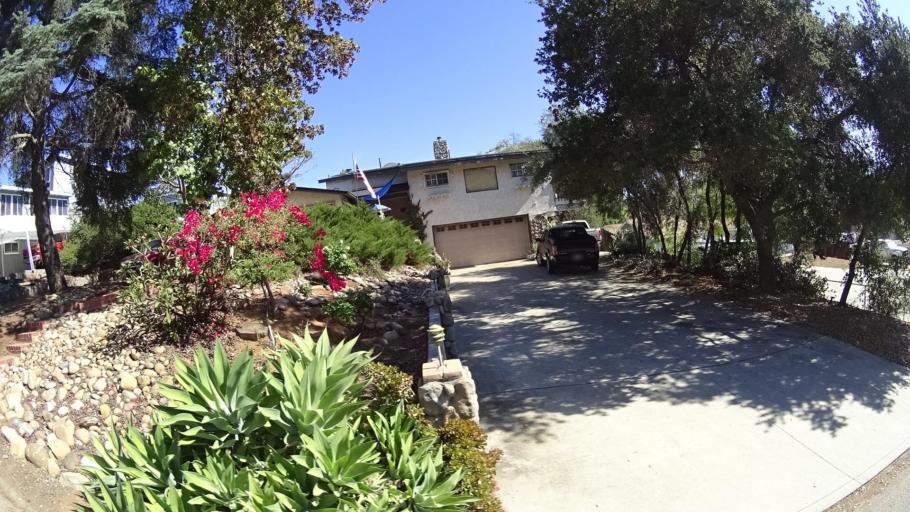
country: US
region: California
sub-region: San Diego County
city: Winter Gardens
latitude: 32.8319
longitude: -116.9339
